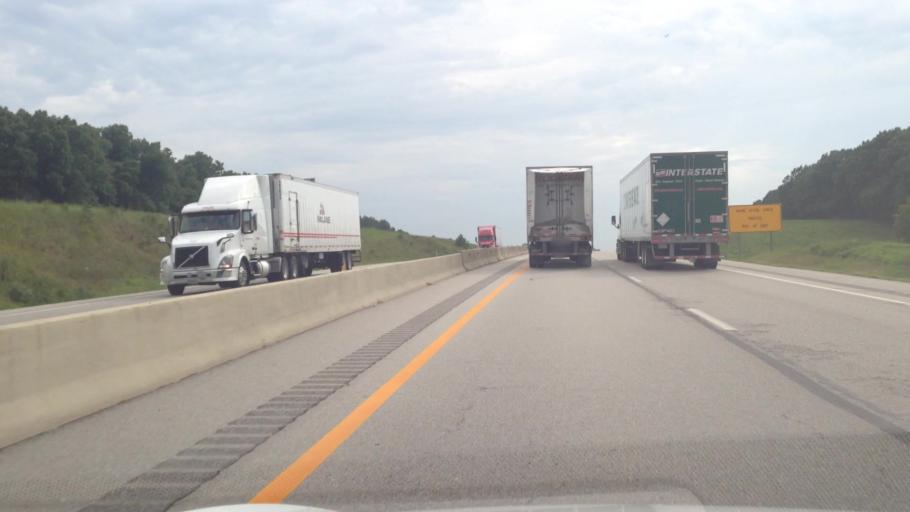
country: US
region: Kansas
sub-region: Cherokee County
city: Galena
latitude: 36.9827
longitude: -94.6350
